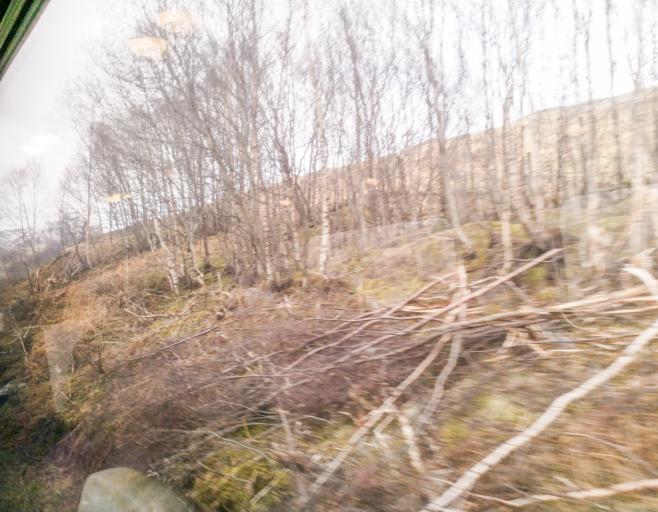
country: GB
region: Scotland
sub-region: Highland
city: Spean Bridge
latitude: 56.7848
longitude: -4.7320
